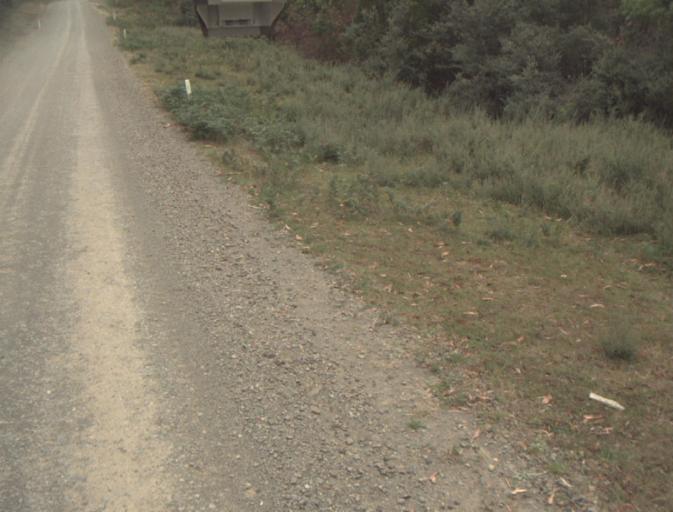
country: AU
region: Tasmania
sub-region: Dorset
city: Scottsdale
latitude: -41.4414
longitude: 147.5158
